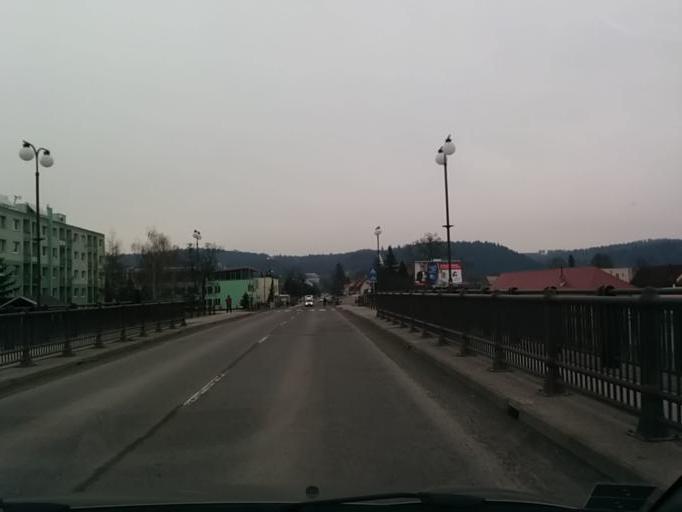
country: SK
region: Banskobystricky
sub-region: Okres Banska Bystrica
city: Zvolen
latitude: 48.6154
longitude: 19.1390
